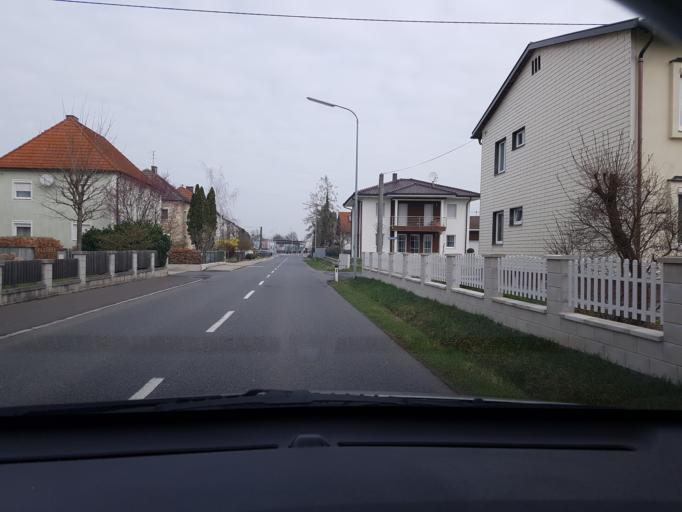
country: AT
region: Upper Austria
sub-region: Politischer Bezirk Linz-Land
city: Asten
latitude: 48.2169
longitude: 14.4200
